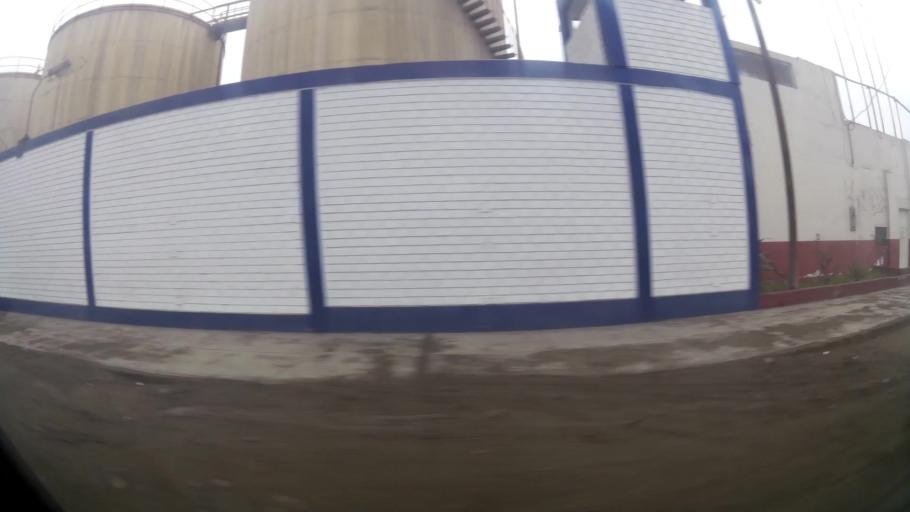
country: PE
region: Lima
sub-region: Provincia de Huaral
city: Chancay
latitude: -11.5779
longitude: -77.2694
